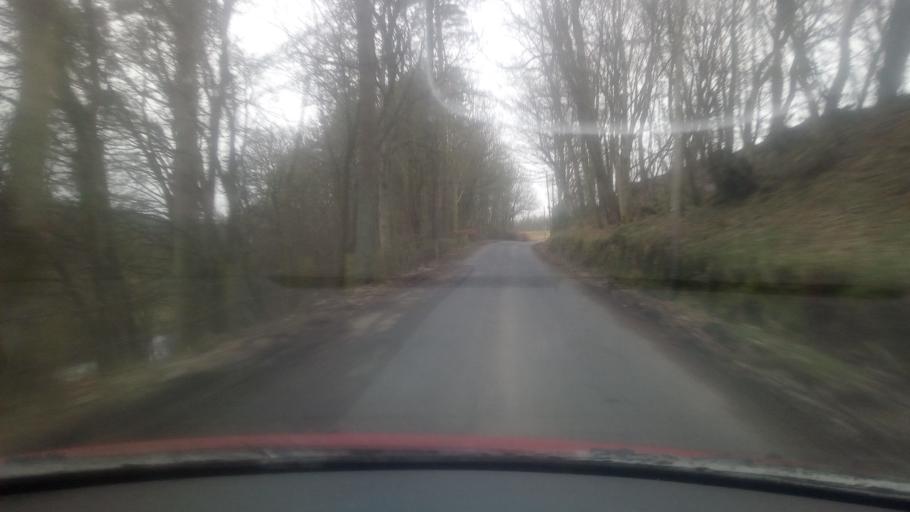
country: GB
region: Scotland
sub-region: The Scottish Borders
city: Hawick
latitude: 55.3853
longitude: -2.6559
